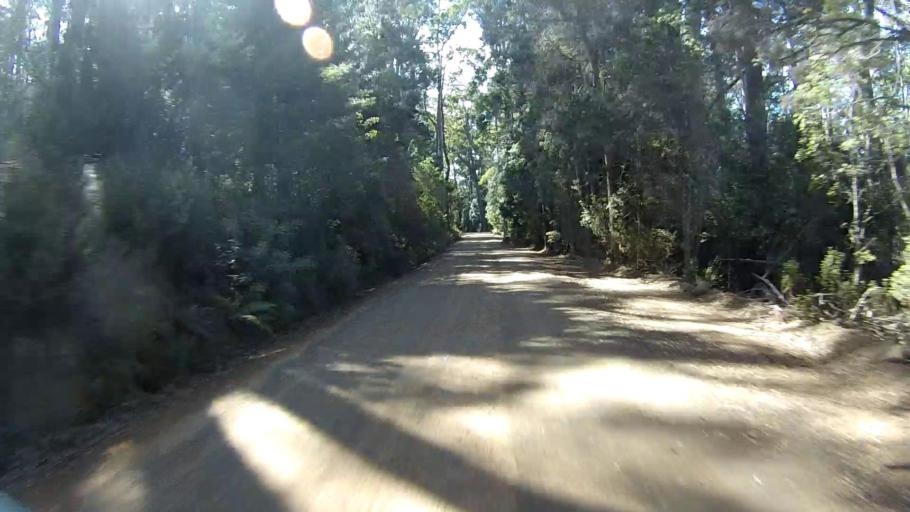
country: AU
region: Tasmania
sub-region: Derwent Valley
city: New Norfolk
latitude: -42.6826
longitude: 146.6512
